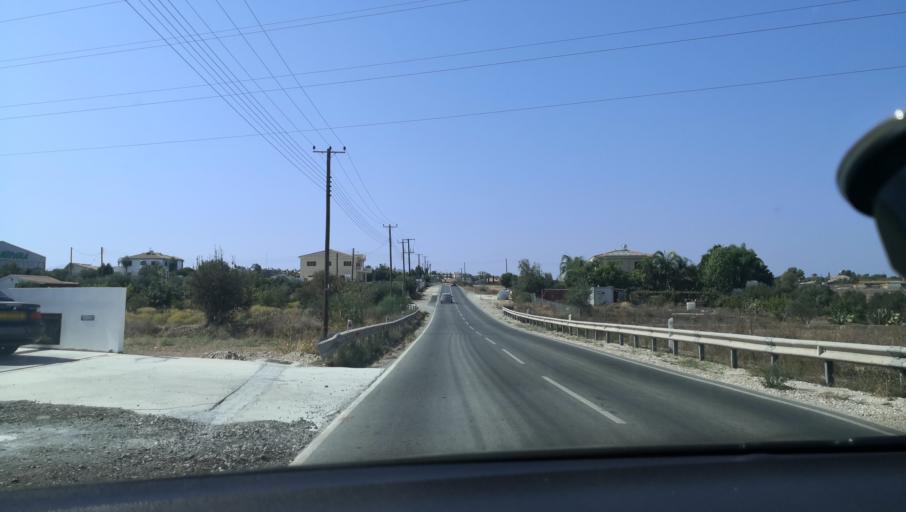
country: CY
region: Lefkosia
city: Kato Deftera
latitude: 35.1219
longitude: 33.2512
